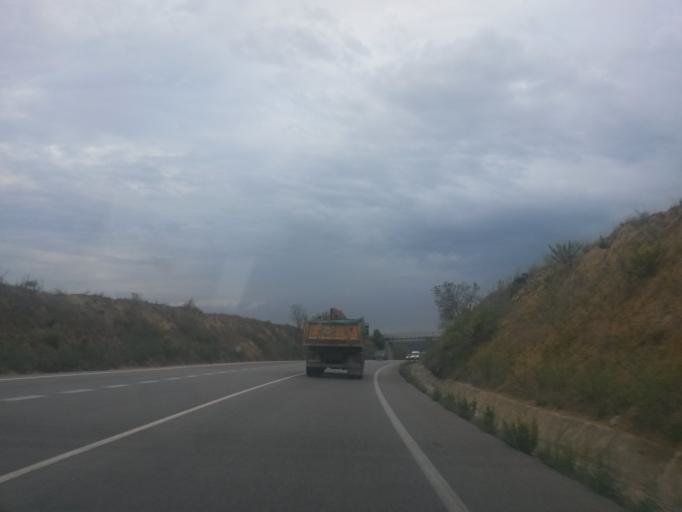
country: ES
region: Catalonia
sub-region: Provincia de Girona
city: Fontcoberta
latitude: 42.1109
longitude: 2.7932
